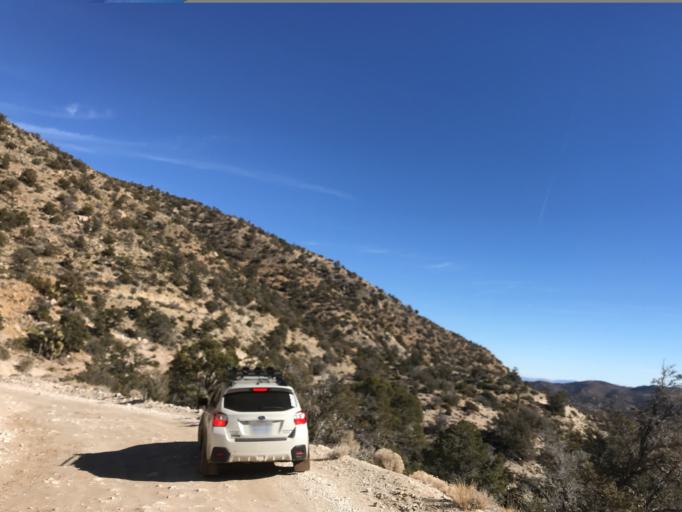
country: US
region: California
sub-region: San Bernardino County
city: Big Bear City
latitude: 34.2335
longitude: -116.6853
